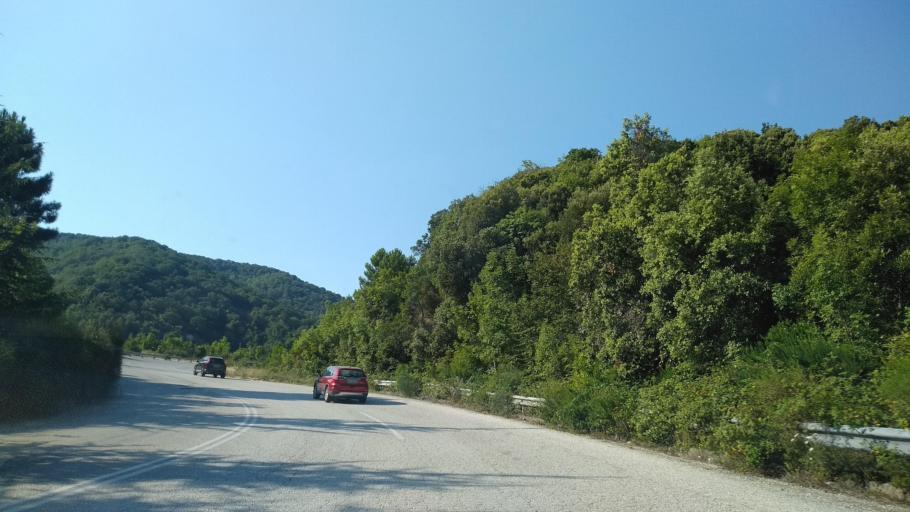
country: GR
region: Central Macedonia
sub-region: Nomos Chalkidikis
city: Stratonion
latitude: 40.5405
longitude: 23.8298
